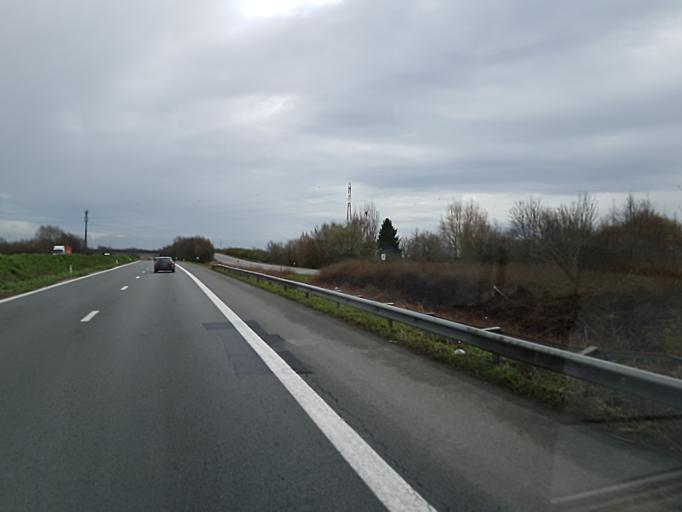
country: BE
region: Flanders
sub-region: Provincie West-Vlaanderen
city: Kortrijk
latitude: 50.7673
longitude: 3.2752
